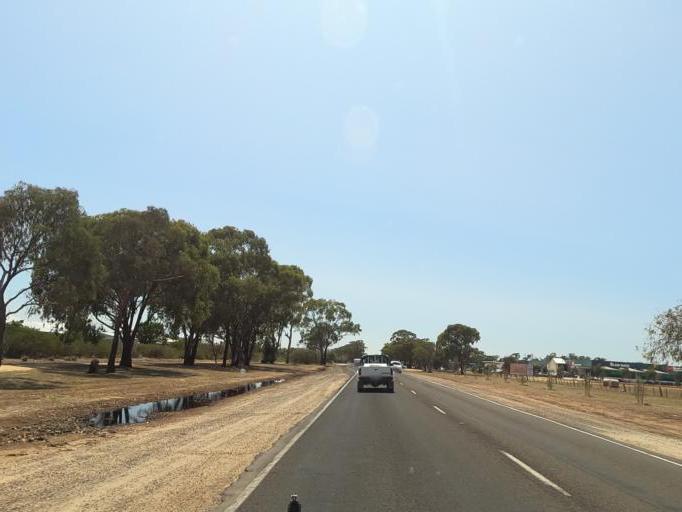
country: AU
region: Victoria
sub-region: Moira
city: Yarrawonga
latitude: -36.0122
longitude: 146.0223
